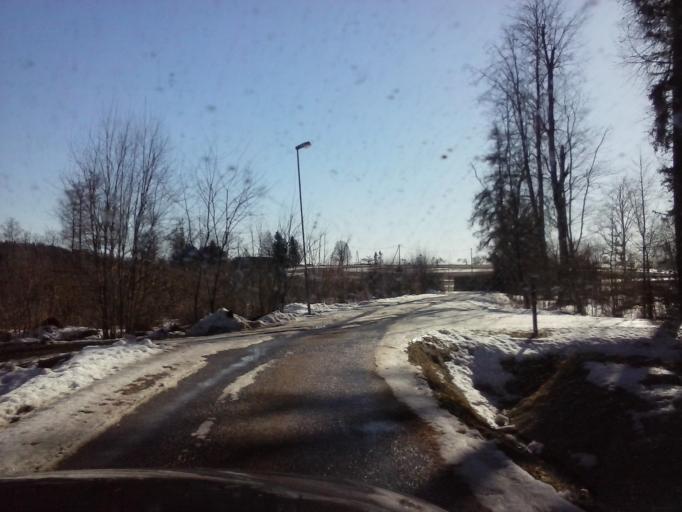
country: EE
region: Laeaene-Virumaa
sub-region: Rakke vald
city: Rakke
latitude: 58.8757
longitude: 26.2734
